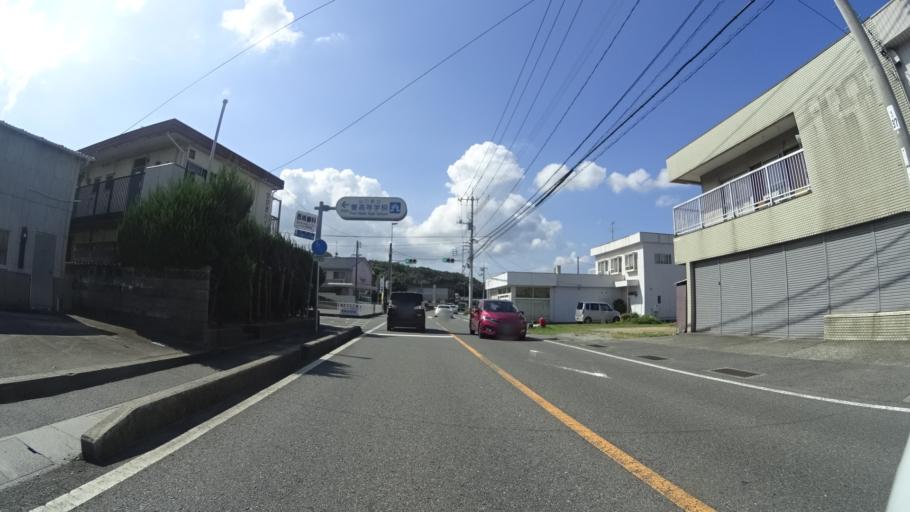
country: JP
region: Yamaguchi
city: Shimonoseki
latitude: 34.1705
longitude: 130.9289
